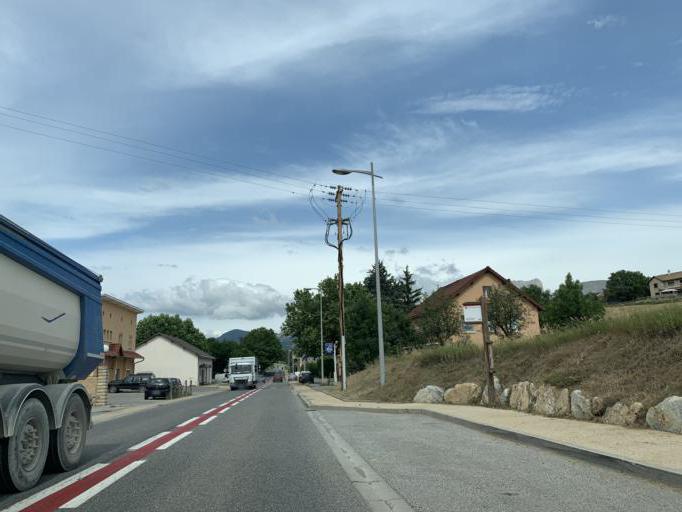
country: FR
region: Provence-Alpes-Cote d'Azur
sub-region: Departement des Hautes-Alpes
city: La Roche-des-Arnauds
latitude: 44.5411
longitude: 6.0144
